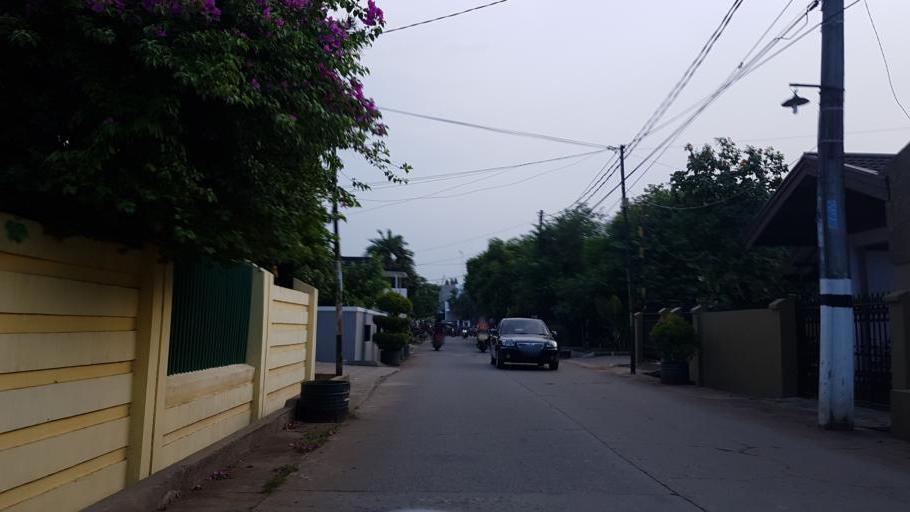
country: ID
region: West Java
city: Bekasi
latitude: -6.2695
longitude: 106.9470
